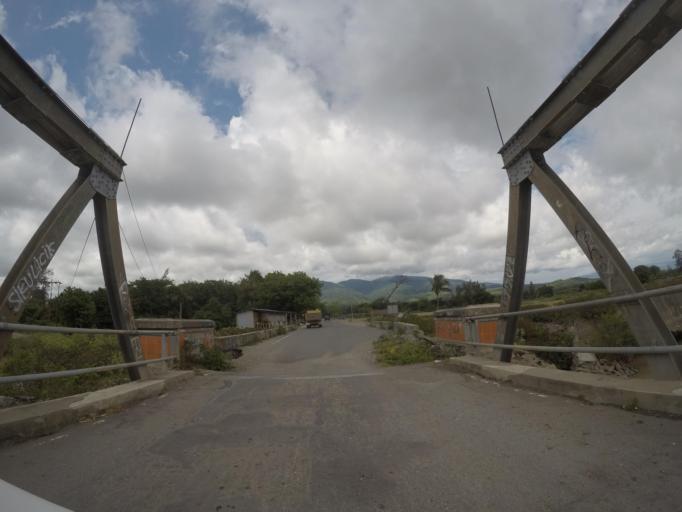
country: TL
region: Liquica
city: Maubara
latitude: -8.7416
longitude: 125.1335
